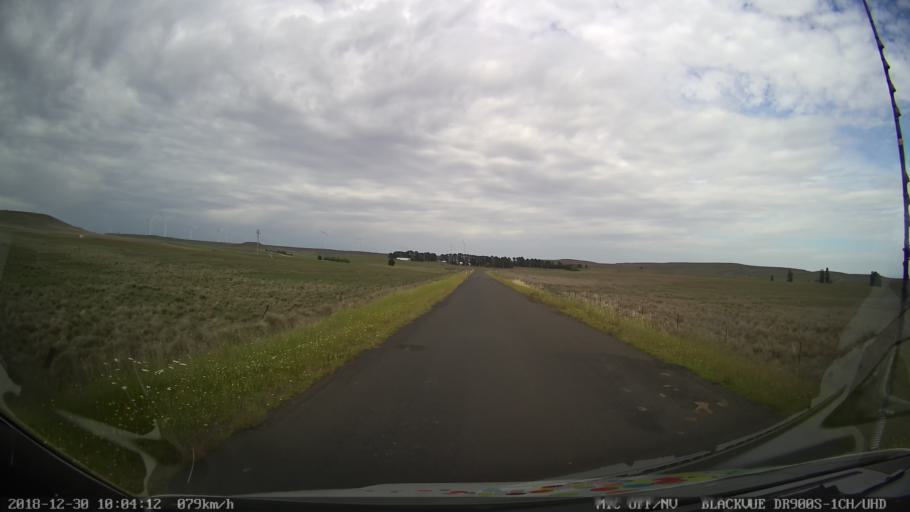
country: AU
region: New South Wales
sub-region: Cooma-Monaro
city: Cooma
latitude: -36.5199
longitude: 149.1486
